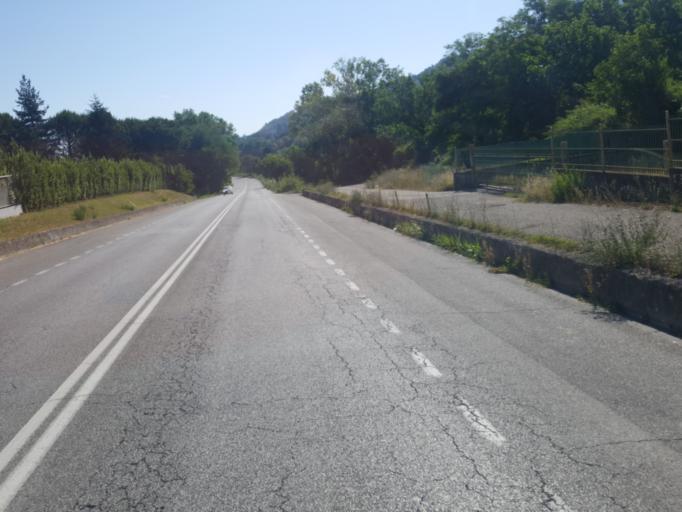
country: IT
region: The Marches
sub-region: Provincia di Pesaro e Urbino
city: Montelabbate
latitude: 43.8450
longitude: 12.7737
